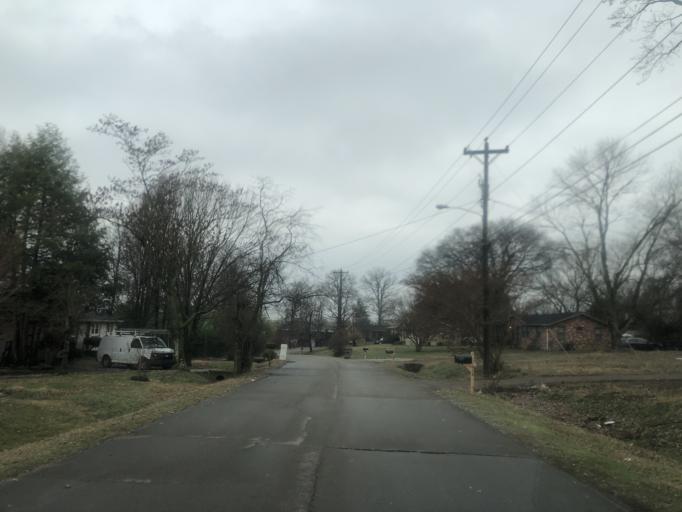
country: US
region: Tennessee
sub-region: Davidson County
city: Lakewood
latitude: 36.1440
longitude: -86.6726
